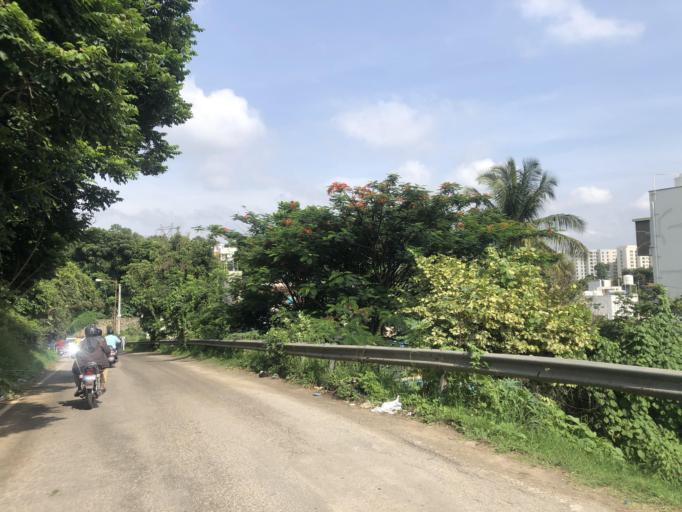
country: IN
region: Karnataka
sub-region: Bangalore Urban
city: Bangalore
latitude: 12.9282
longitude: 77.5329
